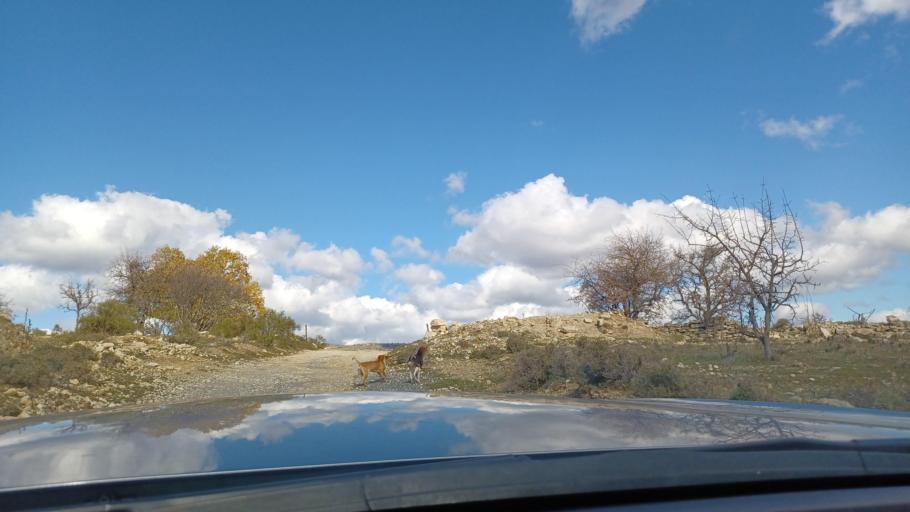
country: CY
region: Limassol
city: Pachna
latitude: 34.8199
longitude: 32.7721
